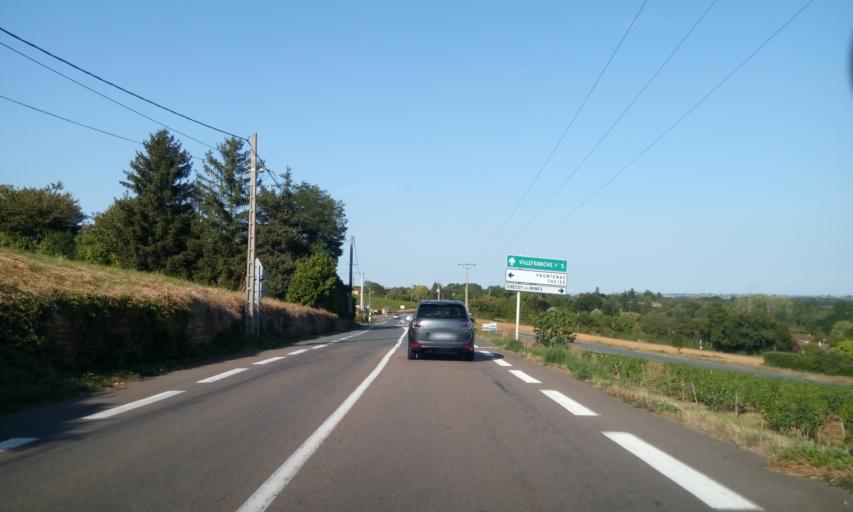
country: FR
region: Rhone-Alpes
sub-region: Departement du Rhone
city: Theize
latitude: 45.9166
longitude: 4.6187
